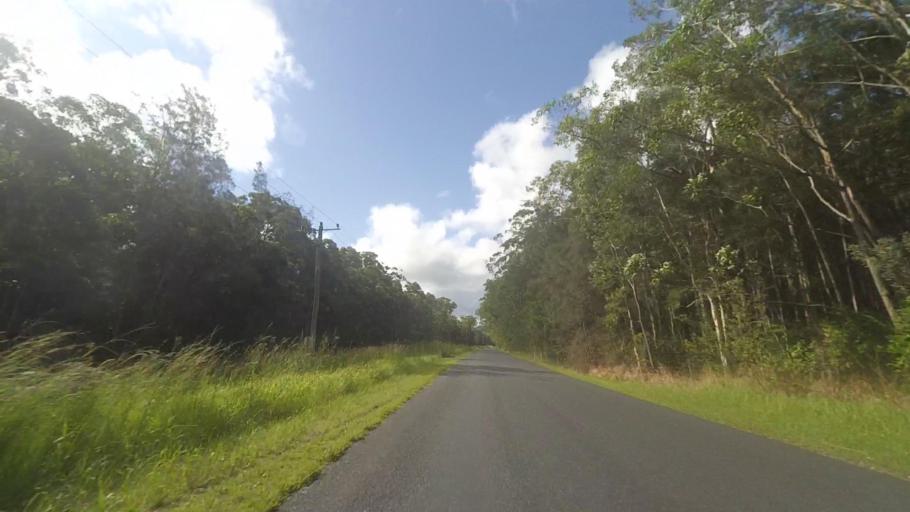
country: AU
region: New South Wales
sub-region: Great Lakes
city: Forster
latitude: -32.4069
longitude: 152.4634
